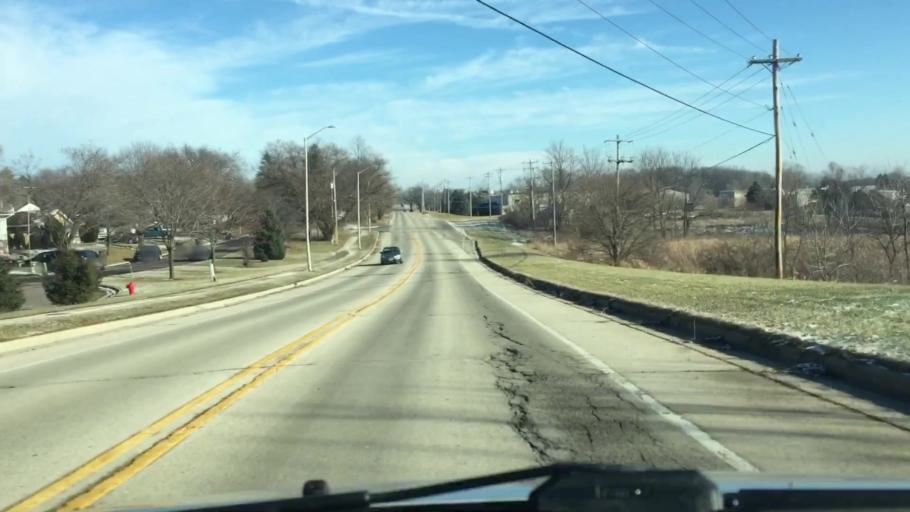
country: US
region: Wisconsin
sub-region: Waukesha County
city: Mukwonago
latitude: 42.8667
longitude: -88.3273
